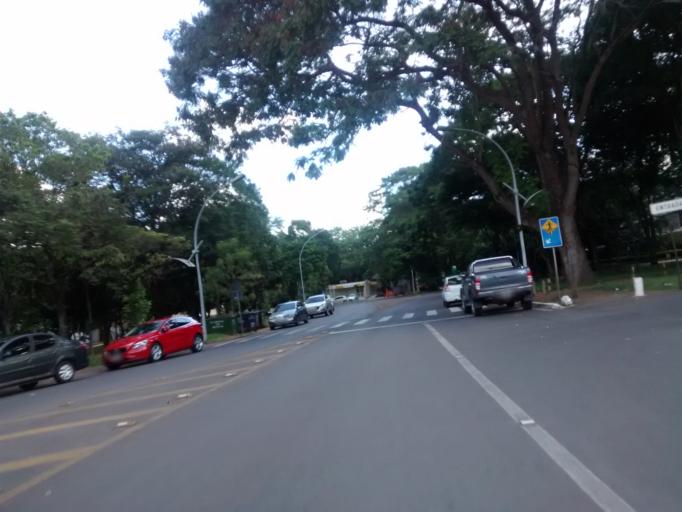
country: BR
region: Federal District
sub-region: Brasilia
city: Brasilia
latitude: -15.8062
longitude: -47.8942
